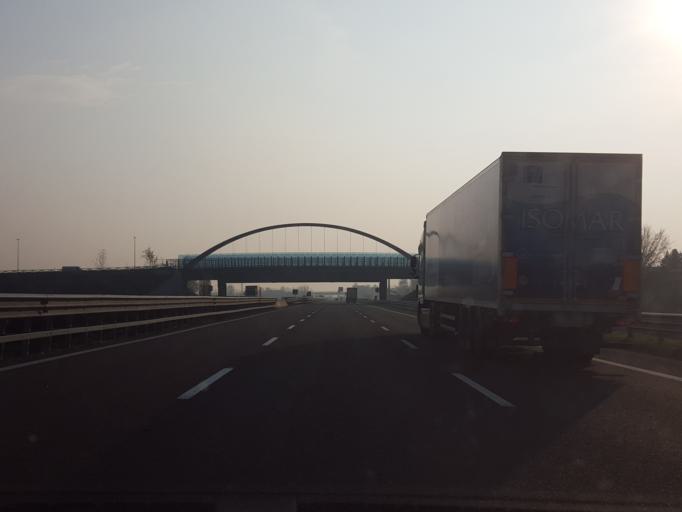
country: IT
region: Veneto
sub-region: Provincia di Treviso
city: Conscio
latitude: 45.6042
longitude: 12.2973
